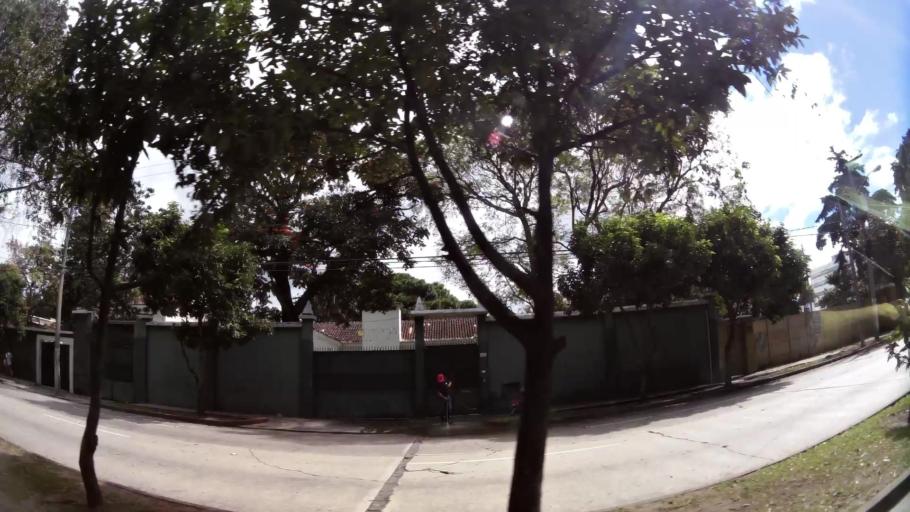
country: GT
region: Guatemala
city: Guatemala City
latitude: 14.6066
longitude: -90.5210
